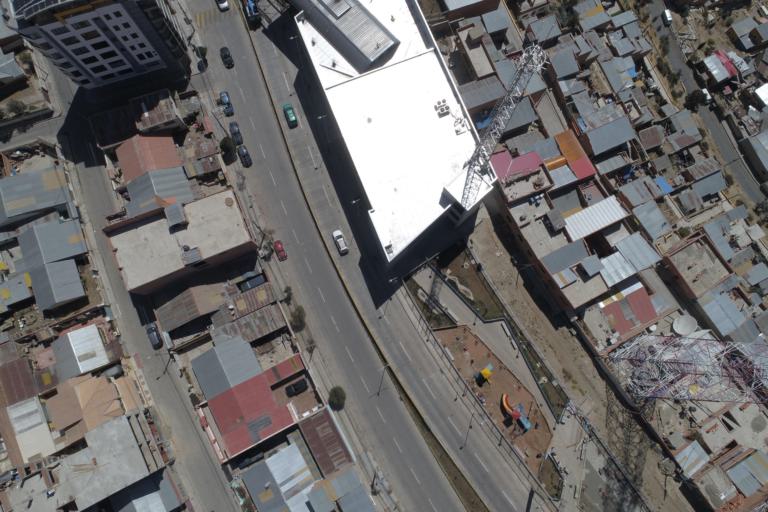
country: BO
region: La Paz
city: La Paz
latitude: -16.5197
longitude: -68.1499
